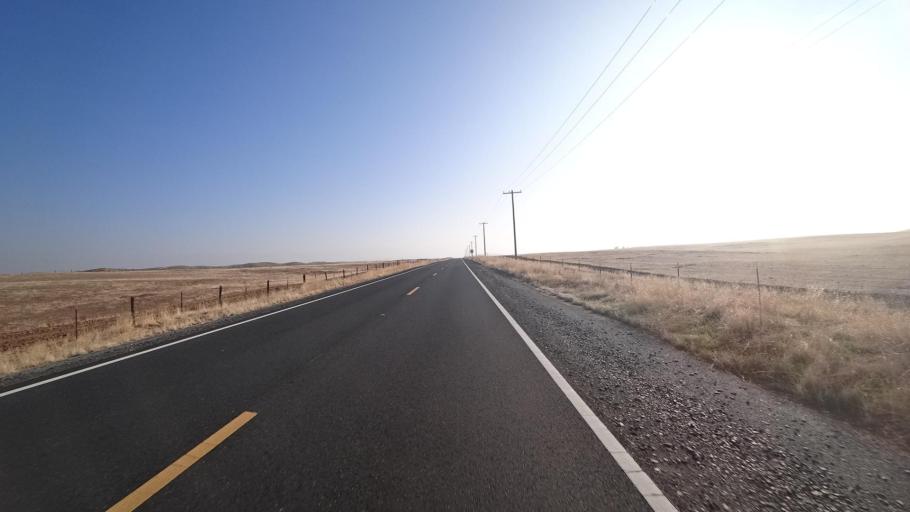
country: US
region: California
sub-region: Tulare County
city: Richgrove
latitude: 35.7620
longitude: -119.0464
